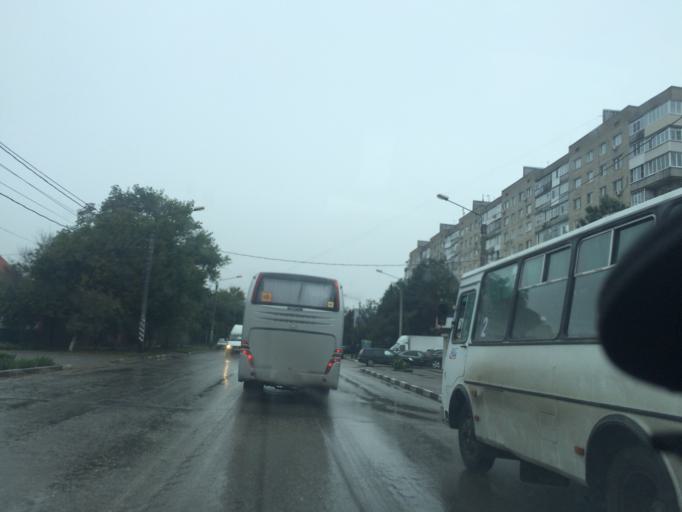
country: RU
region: Rostov
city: Azov
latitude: 47.0932
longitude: 39.4500
